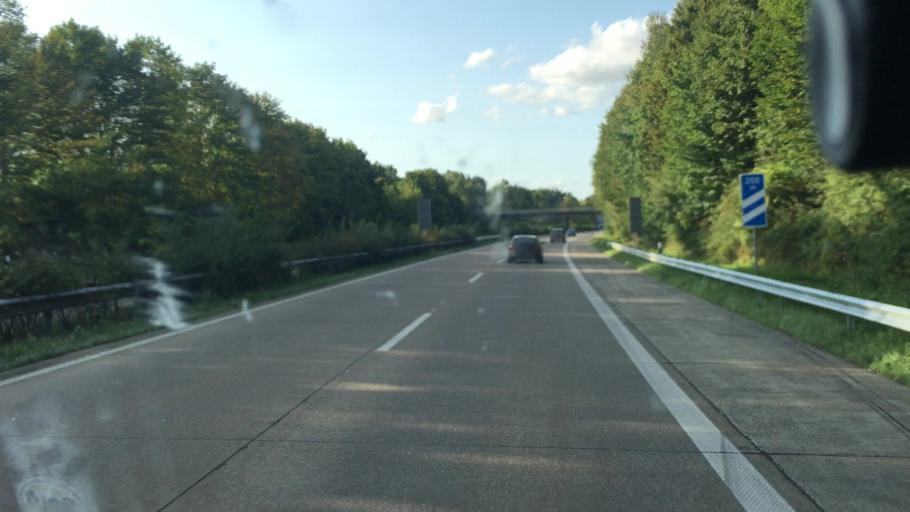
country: DE
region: Lower Saxony
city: Rastede
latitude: 53.2365
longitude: 8.1797
